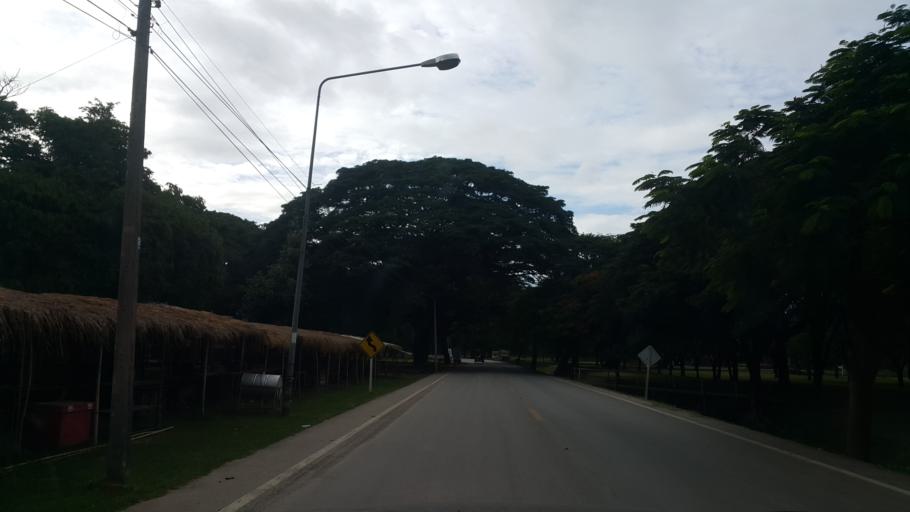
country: TH
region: Sukhothai
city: Ban Na
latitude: 17.0218
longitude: 99.7041
